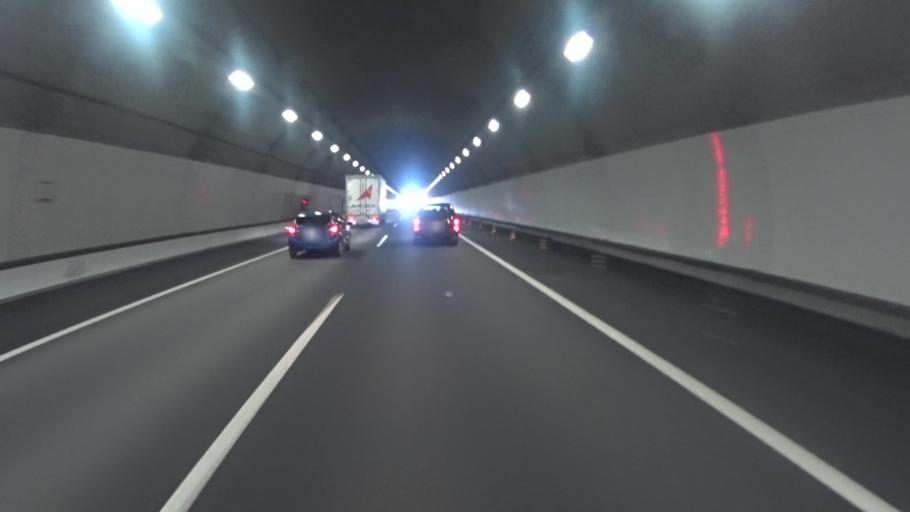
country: JP
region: Mie
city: Kameyama
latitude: 34.9161
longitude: 136.3744
